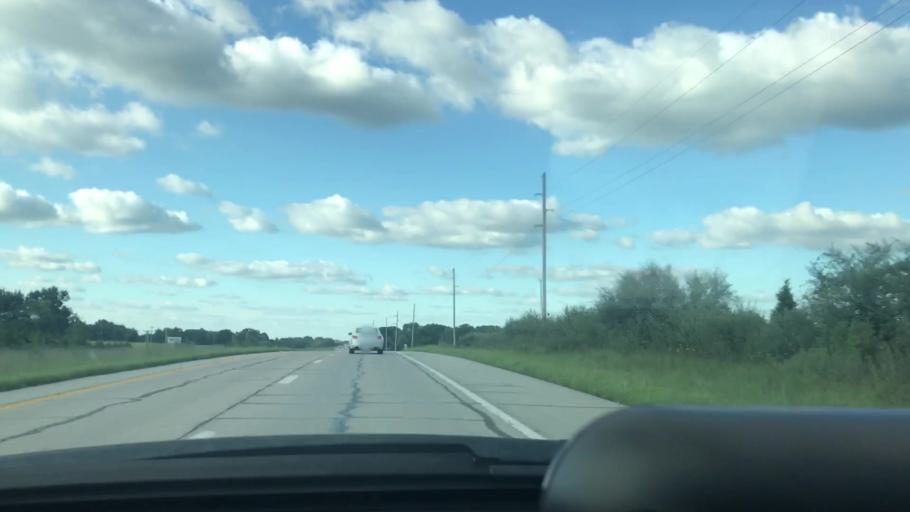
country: US
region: Missouri
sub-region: Pettis County
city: Sedalia
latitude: 38.6223
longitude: -93.2673
